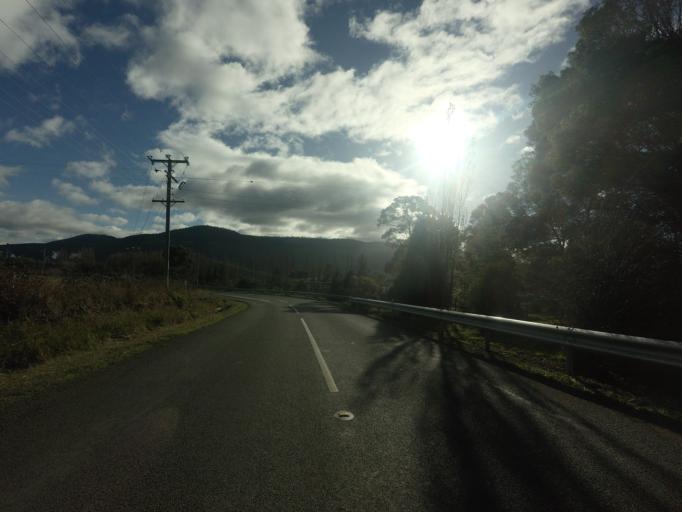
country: AU
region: Tasmania
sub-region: Derwent Valley
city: New Norfolk
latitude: -42.7841
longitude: 147.1170
